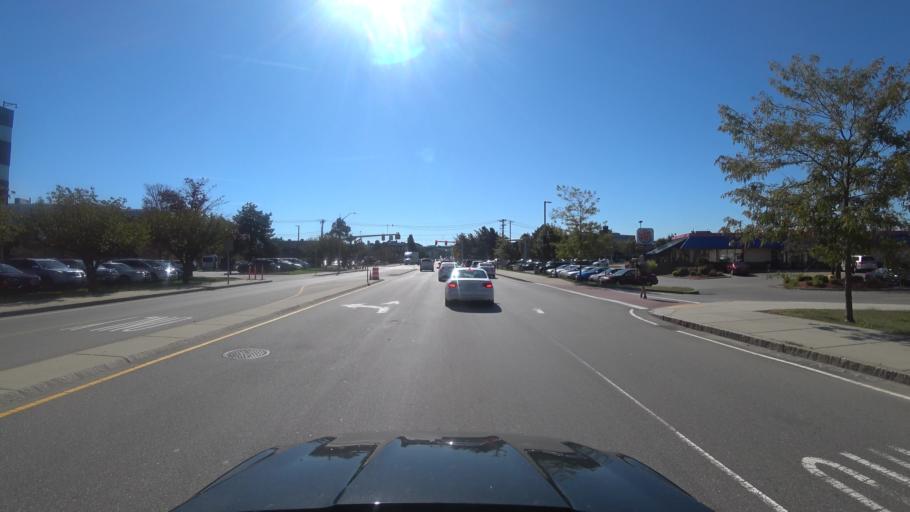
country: US
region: Massachusetts
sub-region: Suffolk County
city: Chelsea
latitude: 42.3962
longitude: -71.0399
